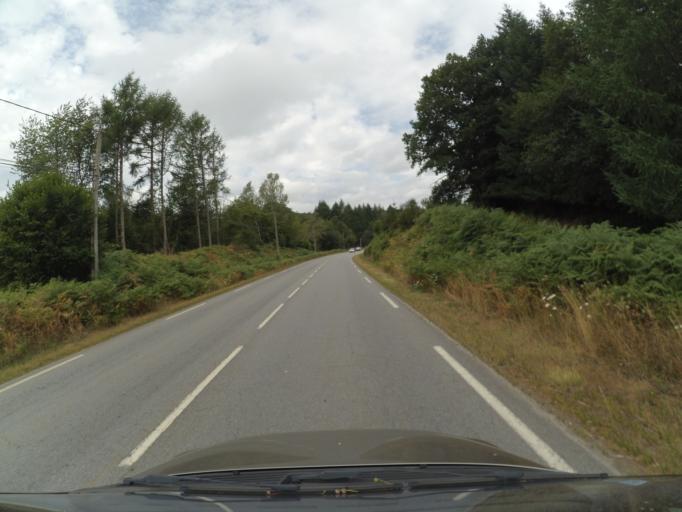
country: FR
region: Limousin
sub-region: Departement de la Correze
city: Ussel
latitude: 45.5785
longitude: 2.2932
